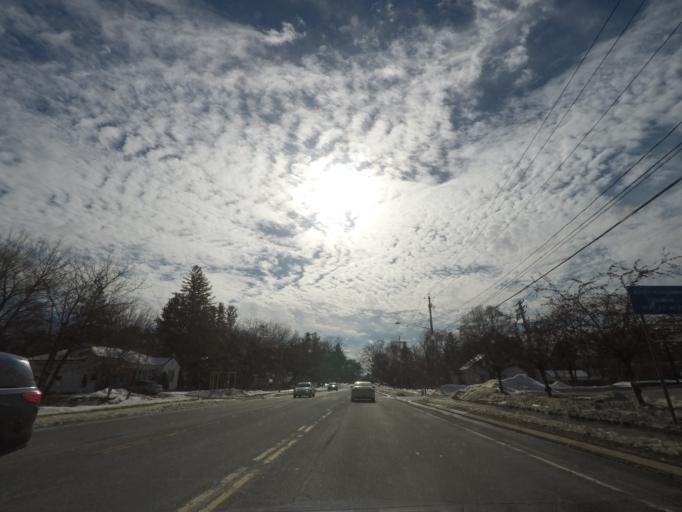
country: US
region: New York
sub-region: Albany County
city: Westmere
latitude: 42.6967
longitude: -73.8889
